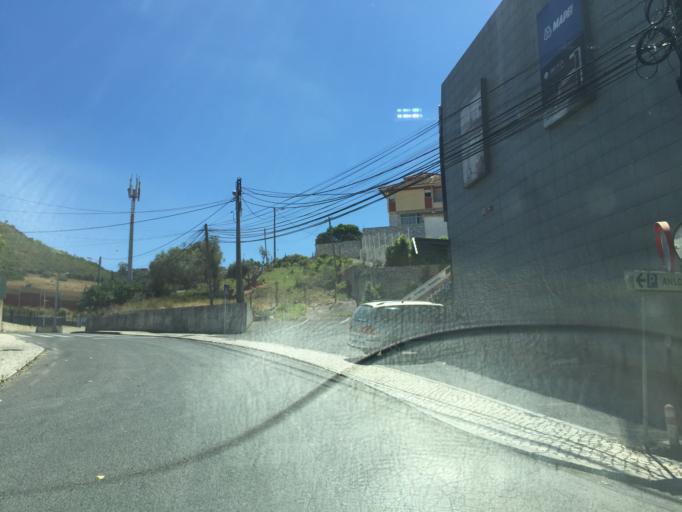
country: PT
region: Lisbon
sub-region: Loures
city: Apelacao
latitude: 38.8132
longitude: -9.1517
